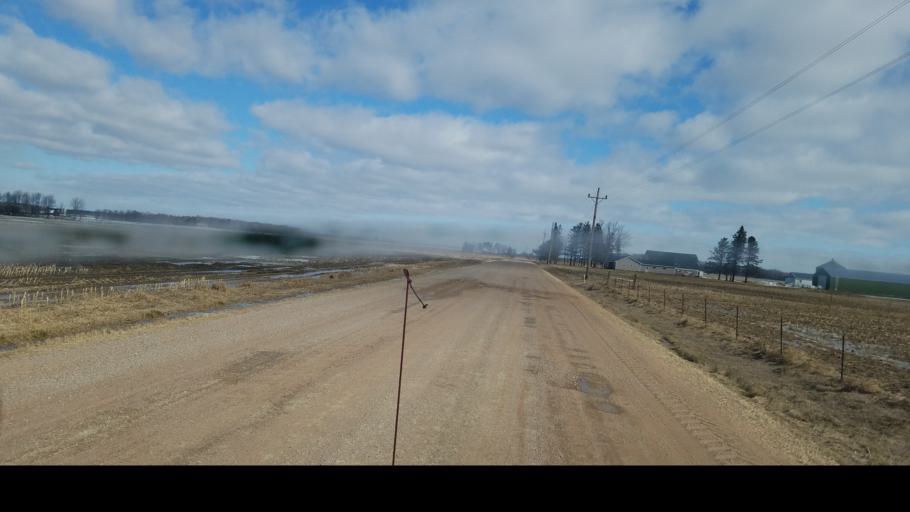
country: US
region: Wisconsin
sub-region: Clark County
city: Loyal
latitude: 44.6720
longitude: -90.4355
